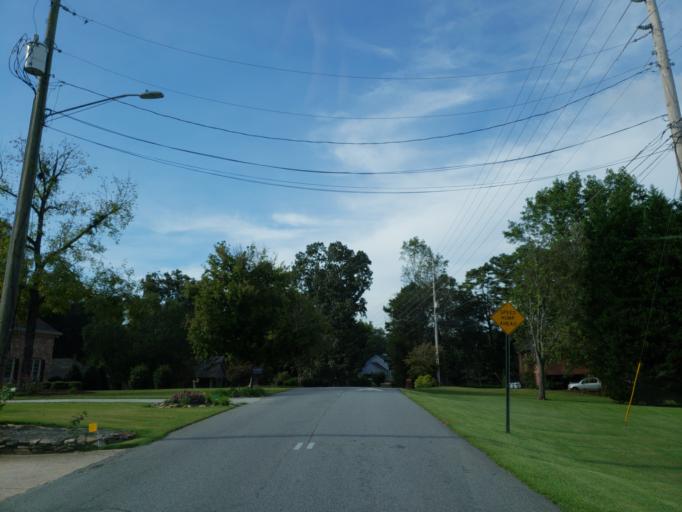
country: US
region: Georgia
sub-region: Cherokee County
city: Woodstock
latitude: 34.0709
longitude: -84.4974
